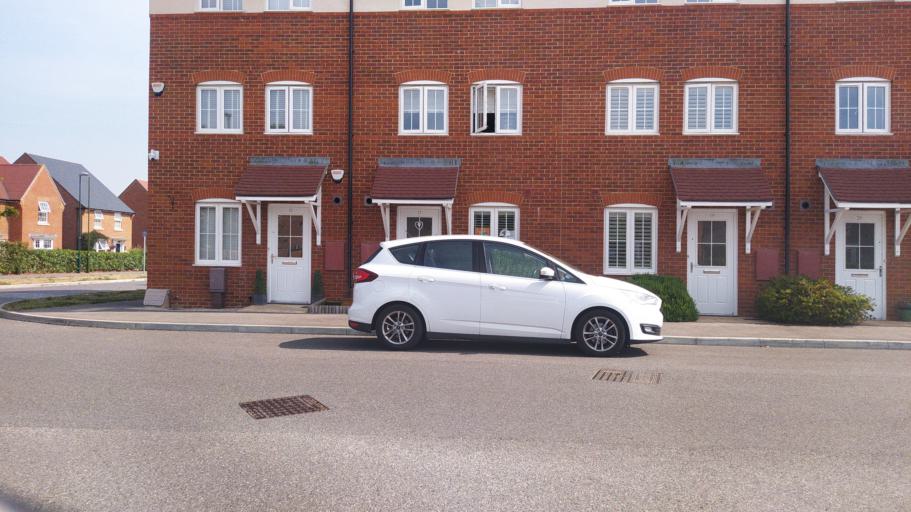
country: GB
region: England
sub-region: West Sussex
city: Barnham
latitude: 50.8014
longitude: -0.6472
